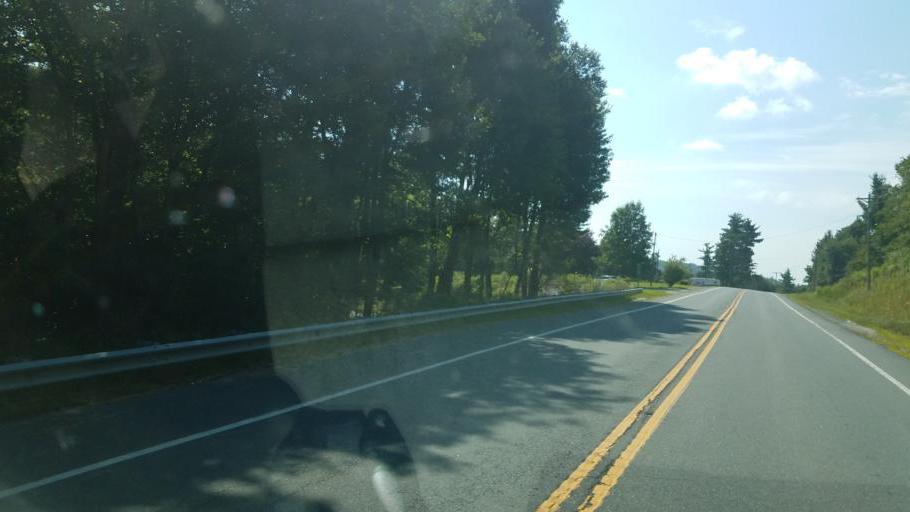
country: US
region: North Carolina
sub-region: Avery County
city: Newland
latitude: 35.9680
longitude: -81.8956
